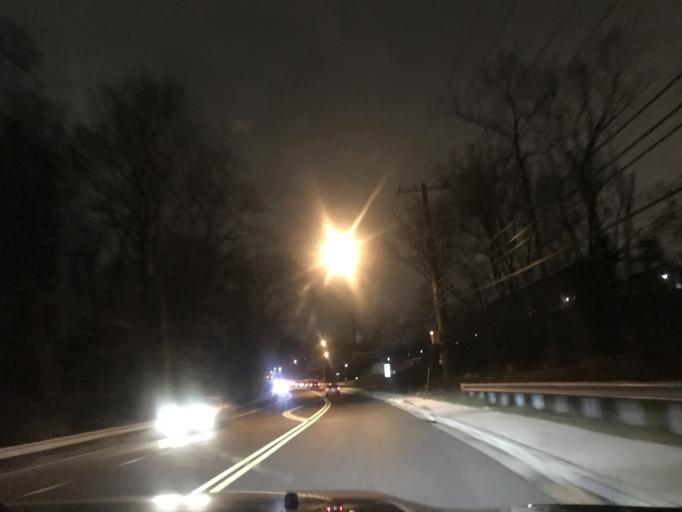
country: US
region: Maryland
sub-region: Prince George's County
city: Temple Hills
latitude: 38.8051
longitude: -76.9590
